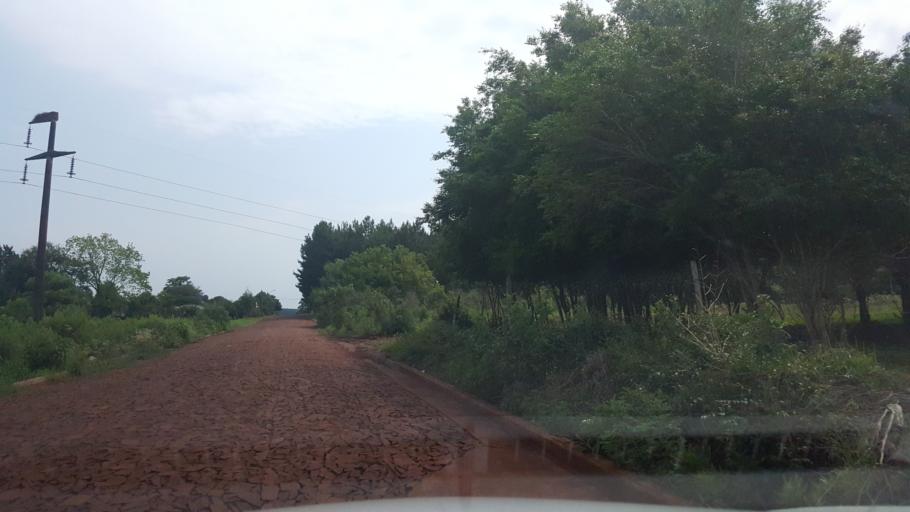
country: AR
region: Misiones
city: Capiovi
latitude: -26.9324
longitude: -55.0510
